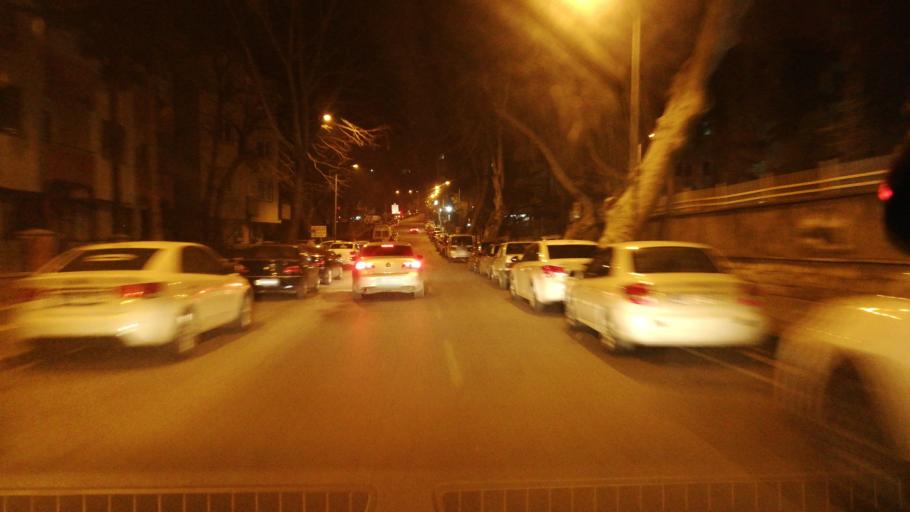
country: TR
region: Kahramanmaras
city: Kahramanmaras
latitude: 37.5887
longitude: 36.9302
